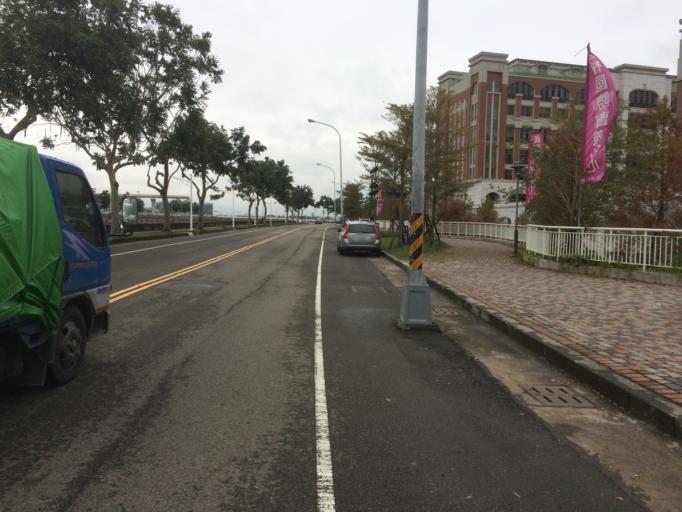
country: TW
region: Taiwan
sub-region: Taichung City
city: Taichung
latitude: 24.1785
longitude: 120.7107
